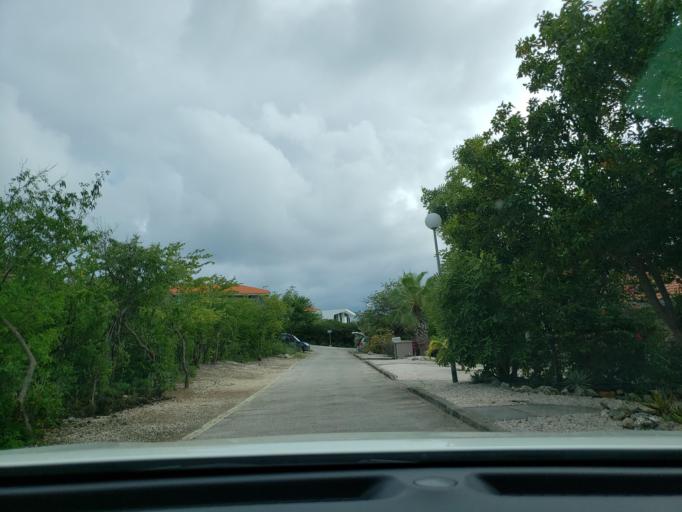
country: CW
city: Dorp Soto
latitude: 12.2008
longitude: -69.0779
